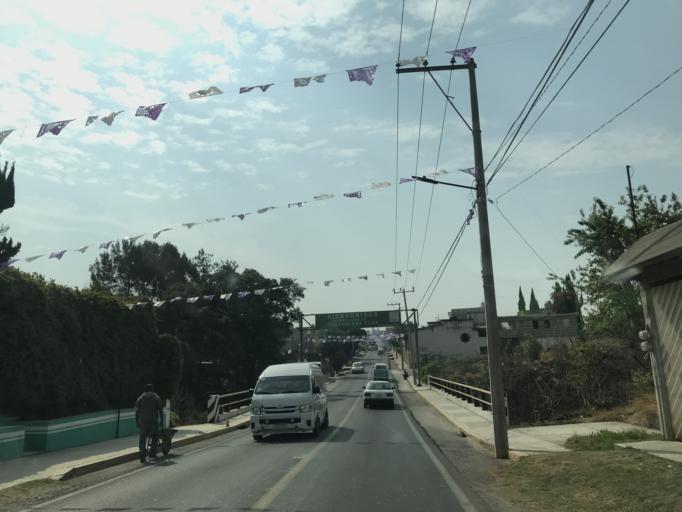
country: MX
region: Tlaxcala
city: Tenancingo
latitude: 19.1521
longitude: -98.2077
